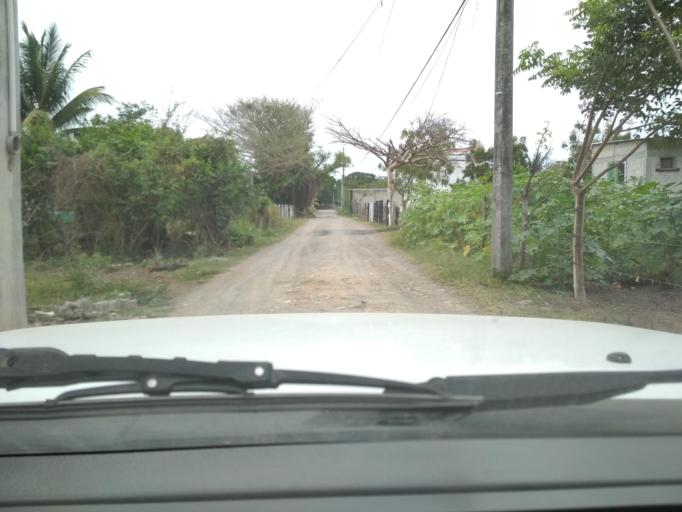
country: MX
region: Veracruz
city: El Tejar
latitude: 19.0722
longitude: -96.1428
